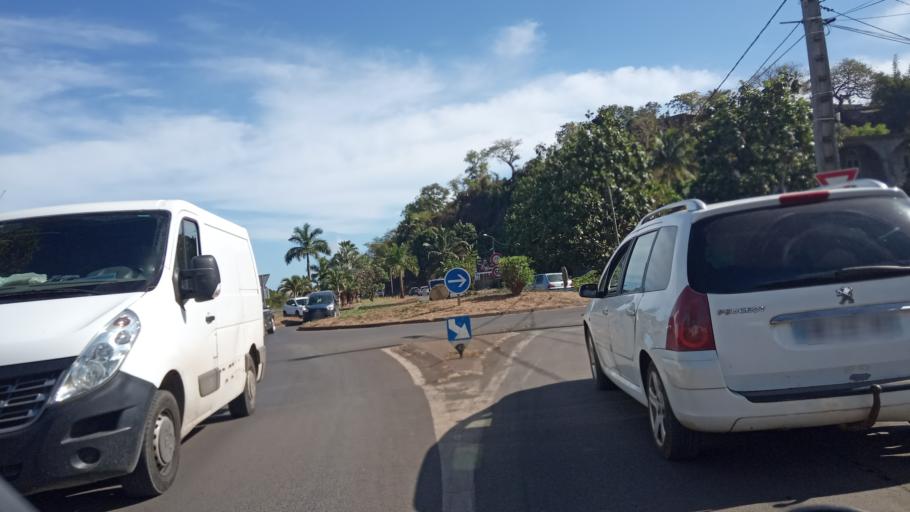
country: YT
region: Mamoudzou
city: Mamoudzou
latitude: -12.7962
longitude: 45.2160
